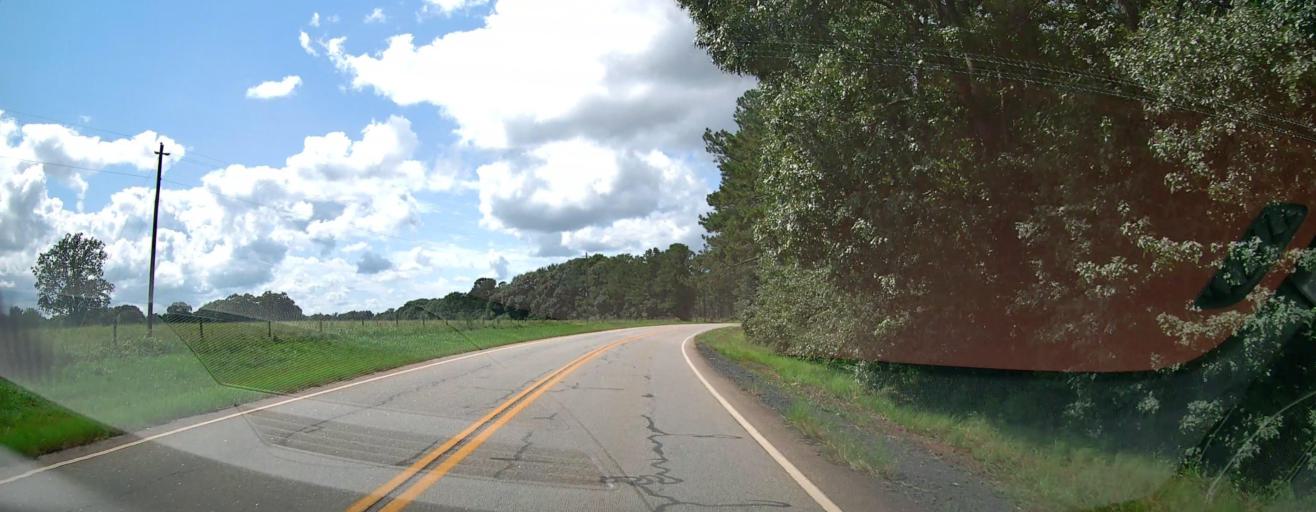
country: US
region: Georgia
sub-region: Lamar County
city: Barnesville
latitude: 32.9068
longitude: -84.1195
